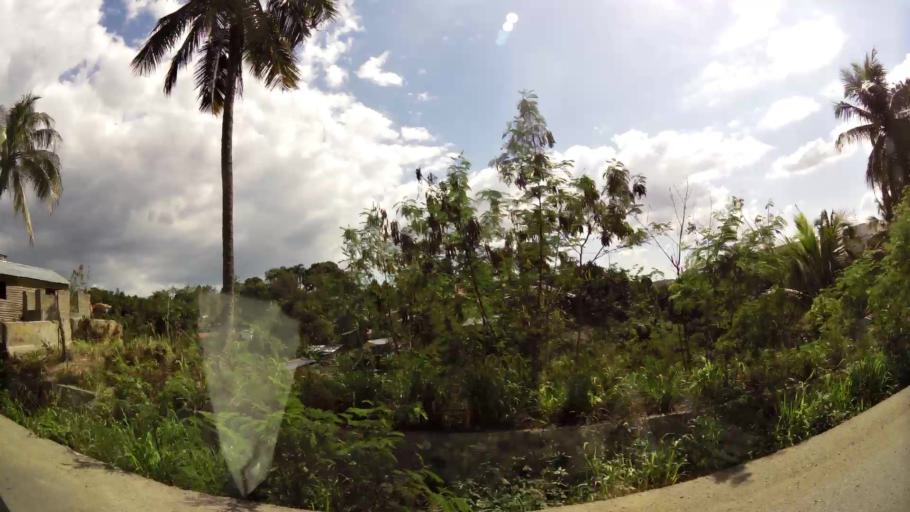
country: DO
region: San Cristobal
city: Bajos de Haina
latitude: 18.4269
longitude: -70.0444
